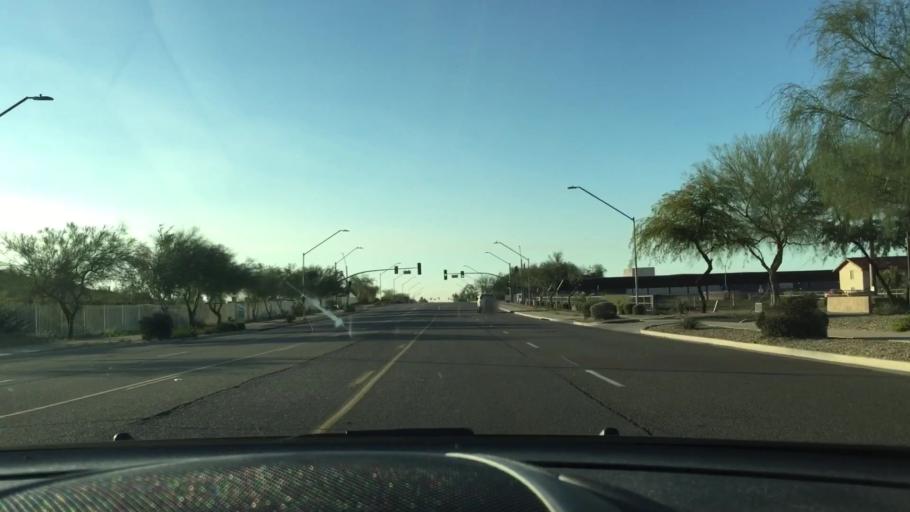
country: US
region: Arizona
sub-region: Maricopa County
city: Sun City
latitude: 33.6940
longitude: -112.2031
